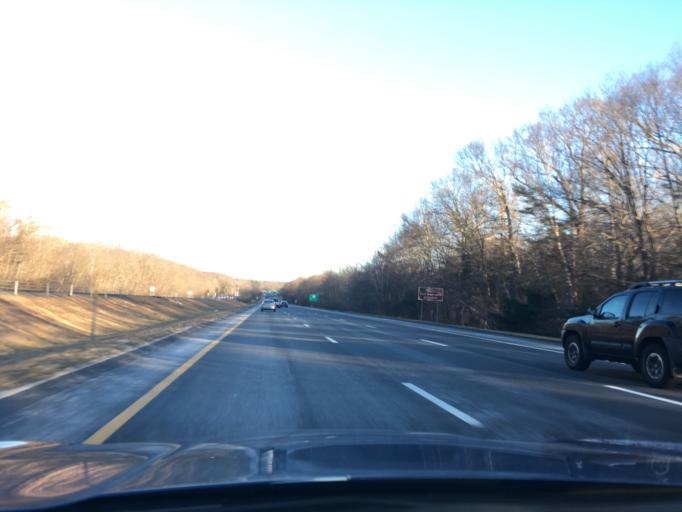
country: US
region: Rhode Island
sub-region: Kent County
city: East Greenwich
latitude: 41.6546
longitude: -71.4890
